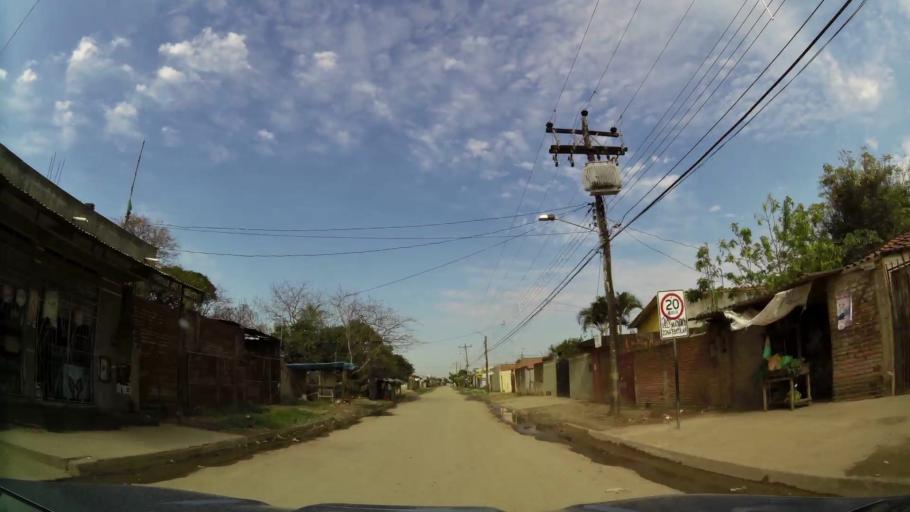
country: BO
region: Santa Cruz
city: Santa Cruz de la Sierra
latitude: -17.7216
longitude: -63.1367
